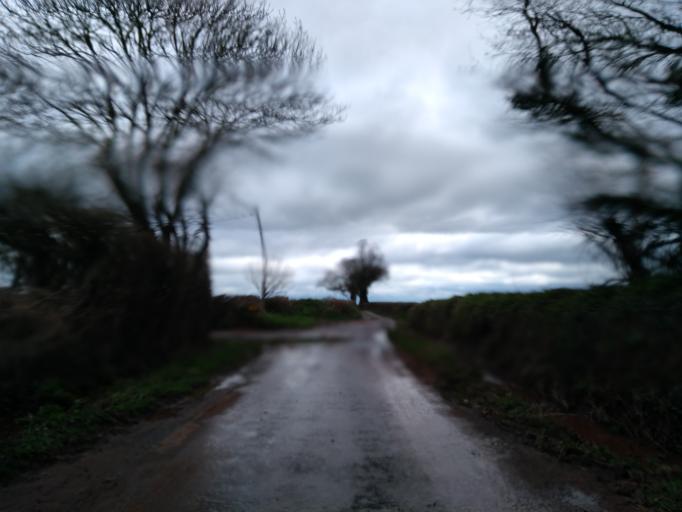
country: GB
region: England
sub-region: Devon
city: Exeter
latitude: 50.7897
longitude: -3.5675
